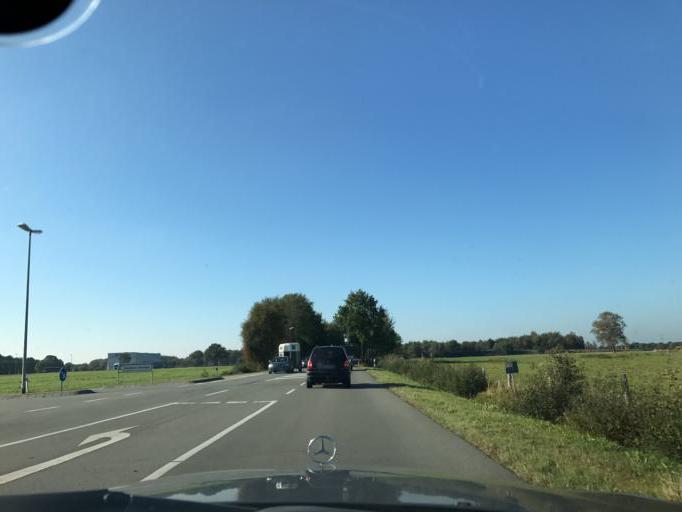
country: DE
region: Lower Saxony
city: Bunde
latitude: 53.1361
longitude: 7.2814
